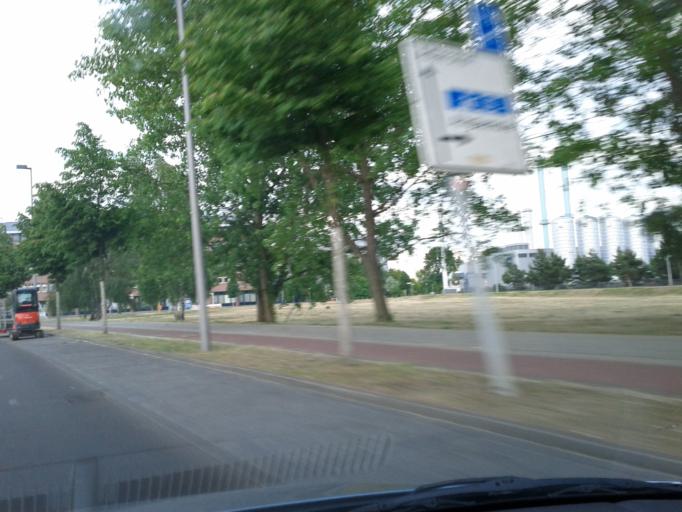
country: DE
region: Berlin
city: Altglienicke
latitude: 52.4285
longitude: 13.5250
